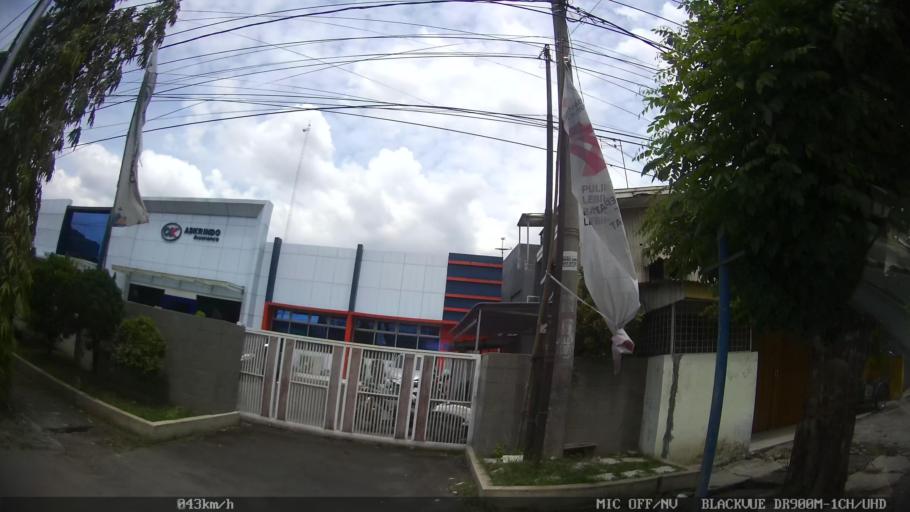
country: ID
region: North Sumatra
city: Medan
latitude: 3.5725
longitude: 98.6606
